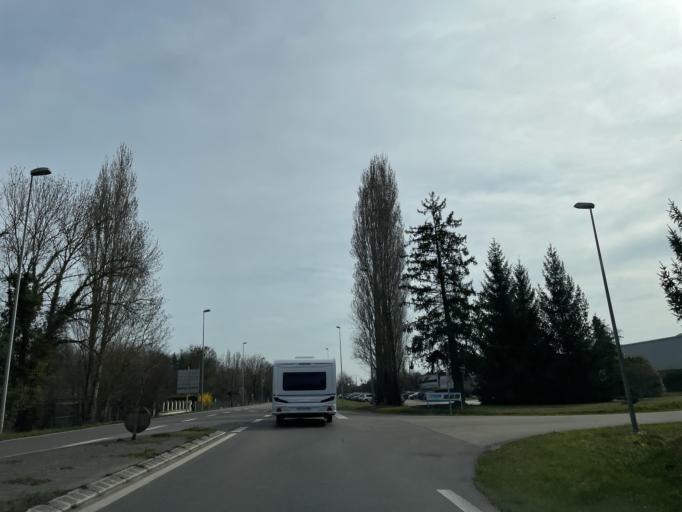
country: FR
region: Champagne-Ardenne
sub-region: Departement de l'Aube
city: Romilly-sur-Seine
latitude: 48.5146
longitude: 3.6651
